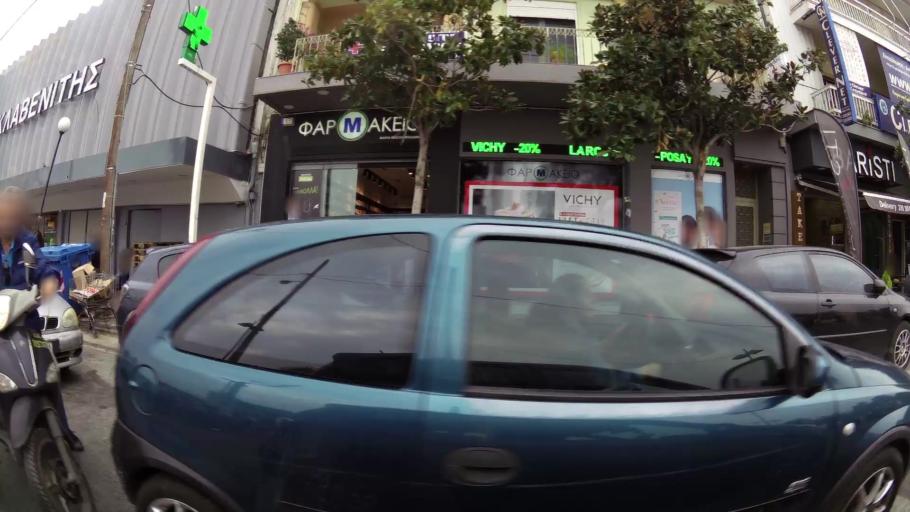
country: GR
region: Attica
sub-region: Nomarchia Athinas
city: Aigaleo
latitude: 37.9920
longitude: 23.6815
